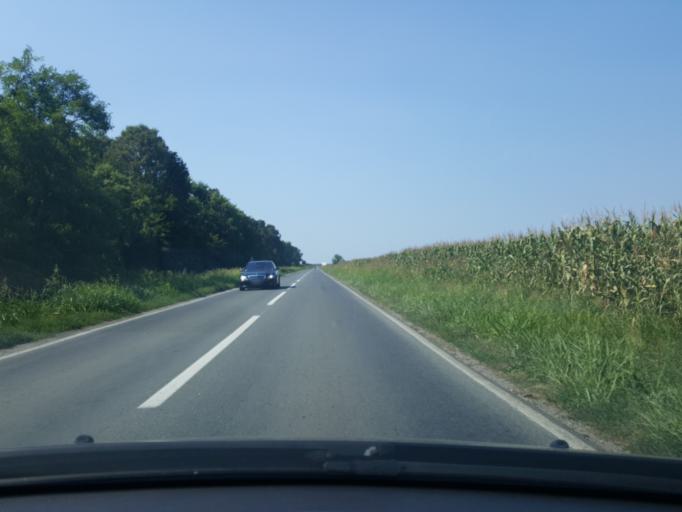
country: RS
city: Platicevo
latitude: 44.8388
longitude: 19.7705
